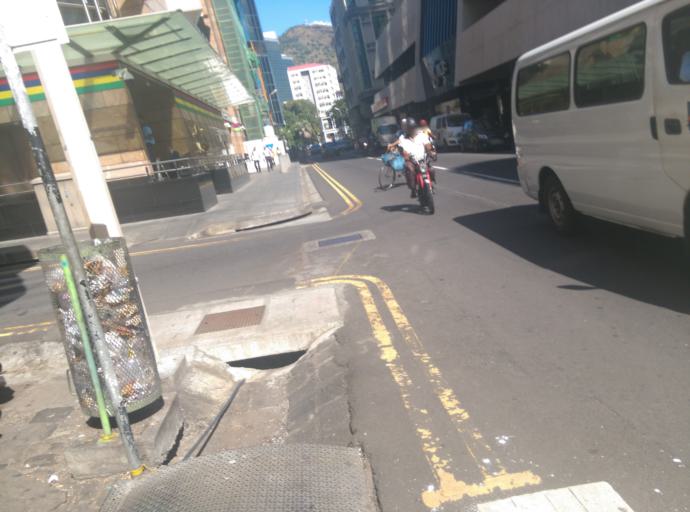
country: MU
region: Port Louis
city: Port Louis
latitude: -20.1612
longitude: 57.5038
